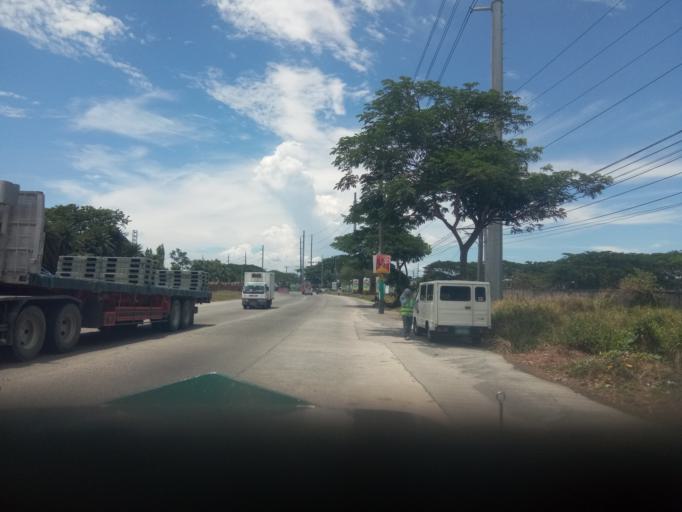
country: PH
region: Calabarzon
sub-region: Province of Cavite
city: Manggahan
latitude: 14.2948
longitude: 120.9244
